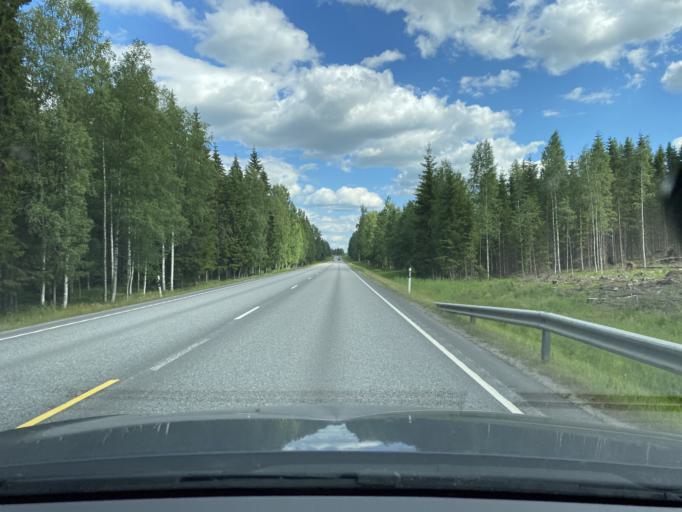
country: FI
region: Satakunta
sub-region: Pori
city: Huittinen
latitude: 61.1209
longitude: 22.8174
